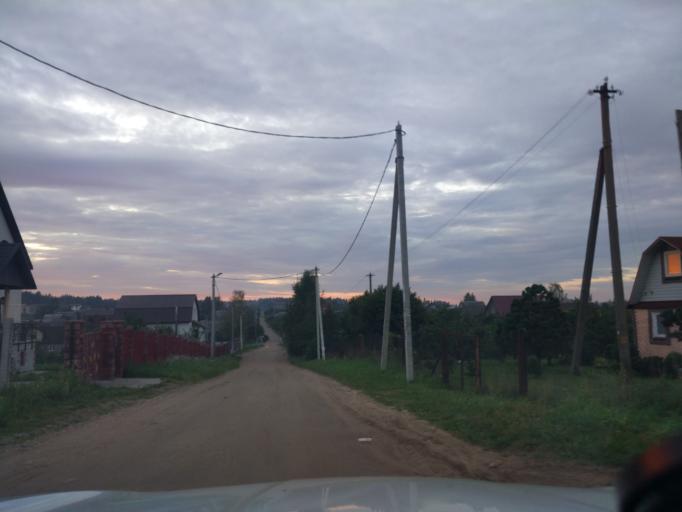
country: BY
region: Minsk
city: Astrashytski Haradok
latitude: 54.0849
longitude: 27.7014
